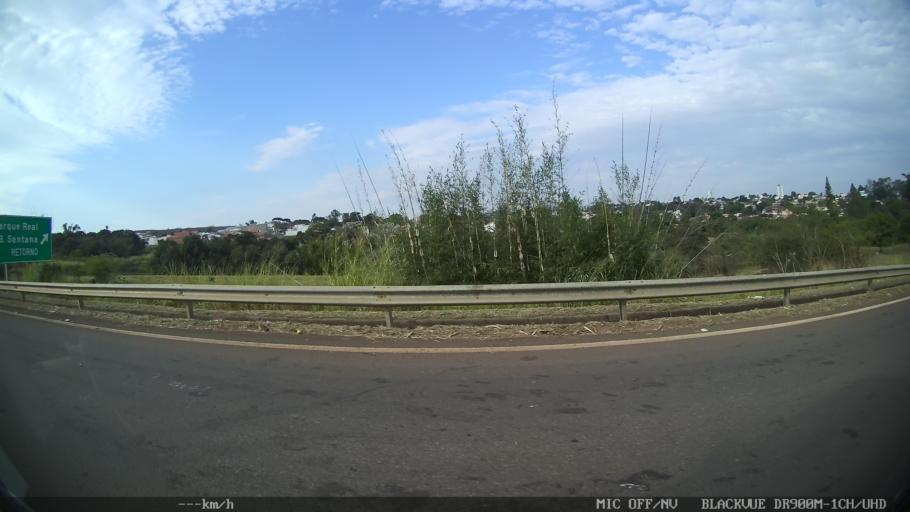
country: BR
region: Sao Paulo
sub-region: Cosmopolis
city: Cosmopolis
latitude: -22.6437
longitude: -47.2085
